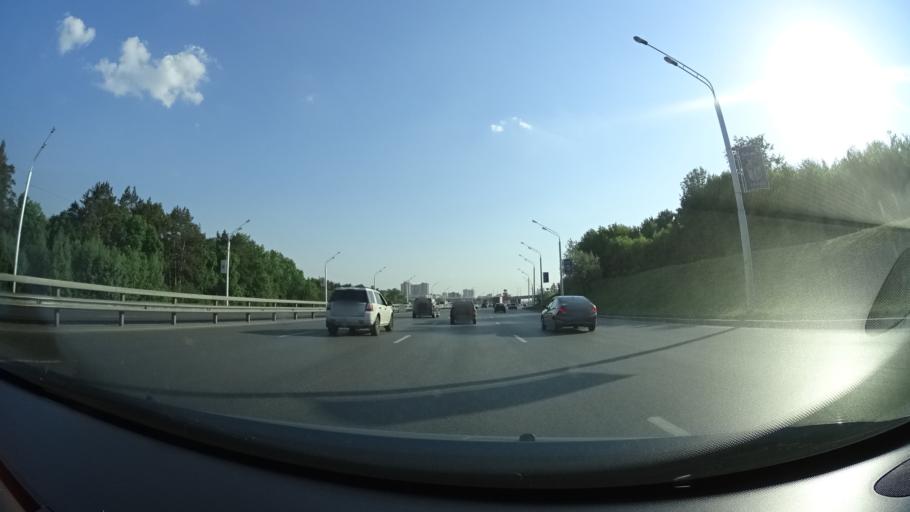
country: RU
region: Bashkortostan
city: Ufa
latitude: 54.7336
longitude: 56.0027
